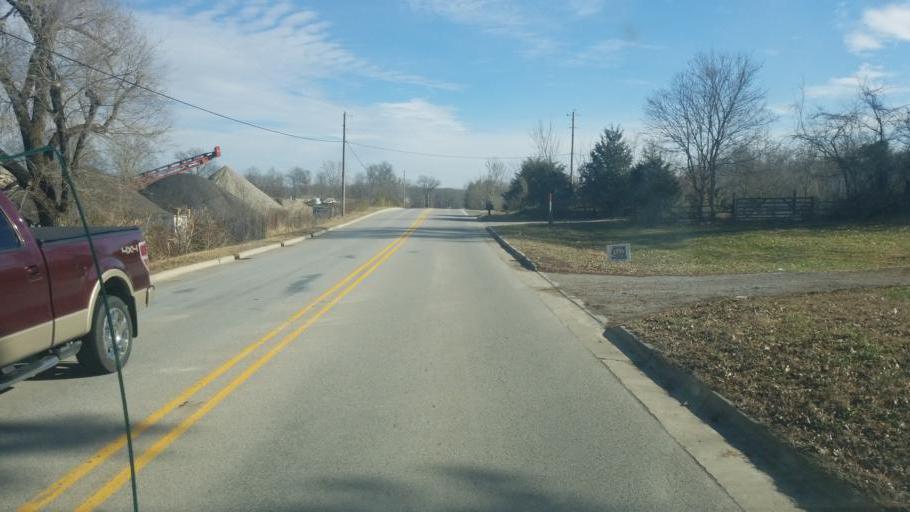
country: US
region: Illinois
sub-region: Jackson County
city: Carbondale
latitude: 37.7007
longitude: -89.1944
